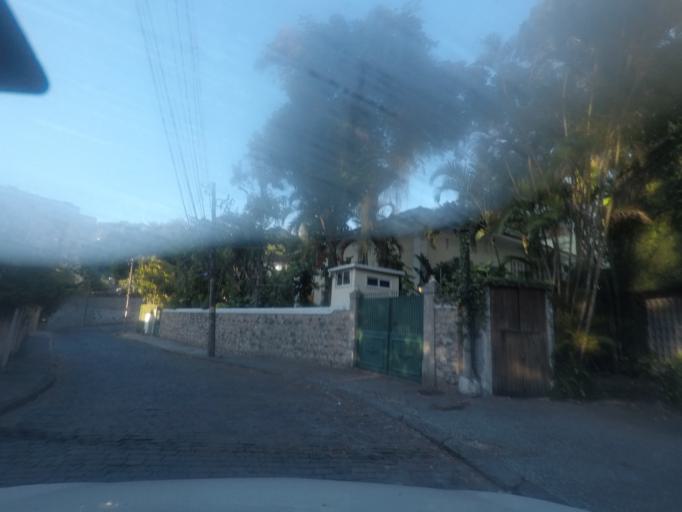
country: BR
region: Rio de Janeiro
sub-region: Rio De Janeiro
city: Rio de Janeiro
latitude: -22.9296
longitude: -43.1890
